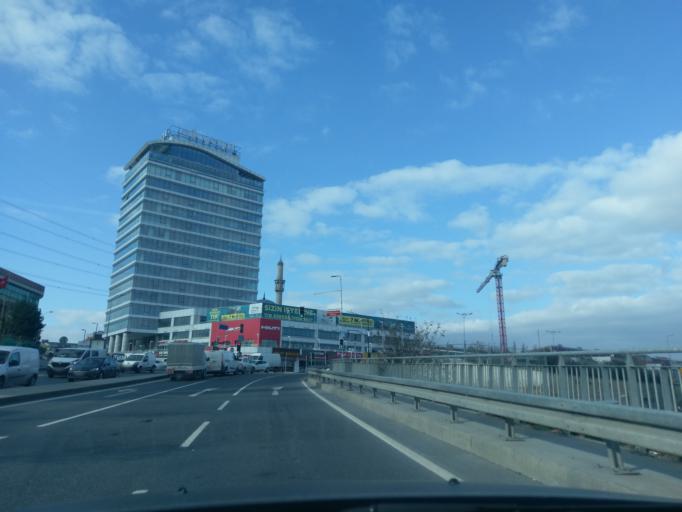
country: TR
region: Istanbul
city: Basaksehir
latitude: 41.0699
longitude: 28.8061
